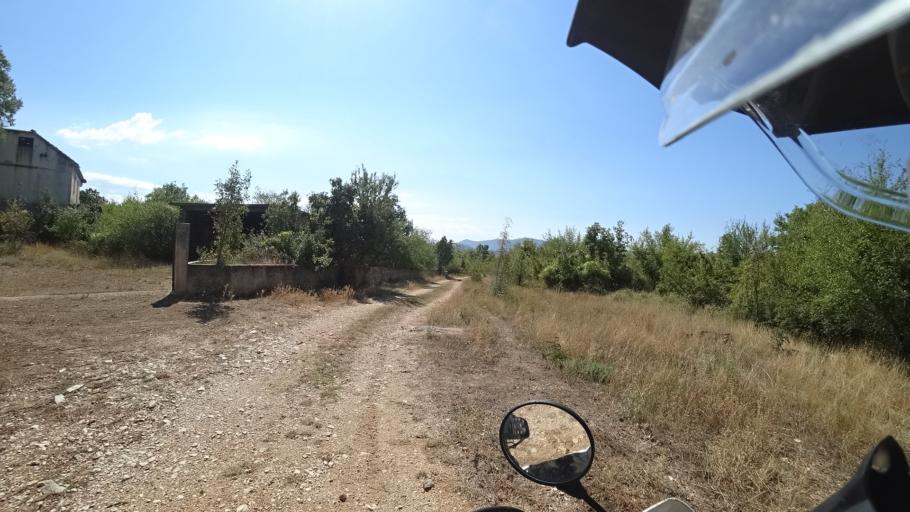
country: HR
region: Sibensko-Kniniska
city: Drnis
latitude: 43.8239
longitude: 16.3120
